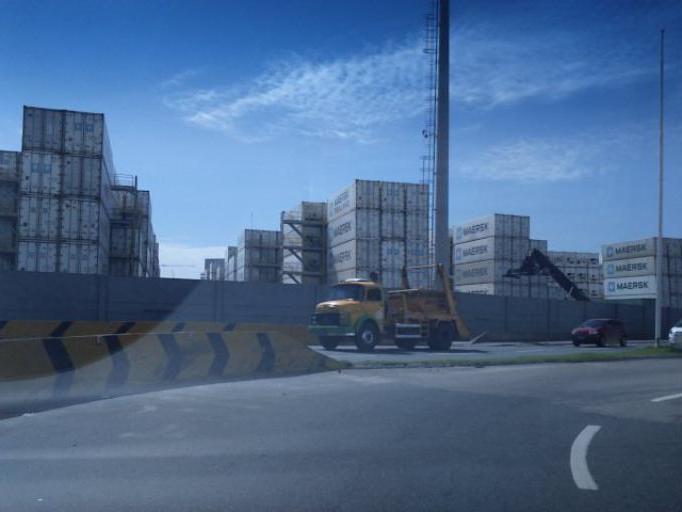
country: BR
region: Santa Catarina
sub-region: Itajai
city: Itajai
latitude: -26.9021
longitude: -48.6636
